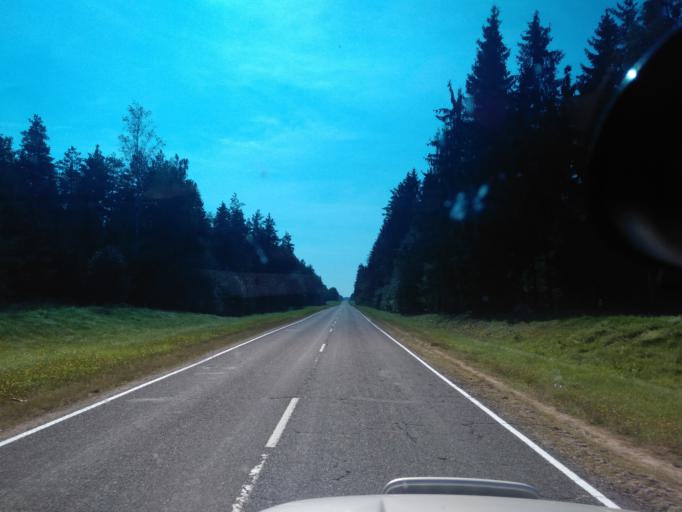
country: BY
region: Minsk
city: Uzda
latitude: 53.3312
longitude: 27.2306
